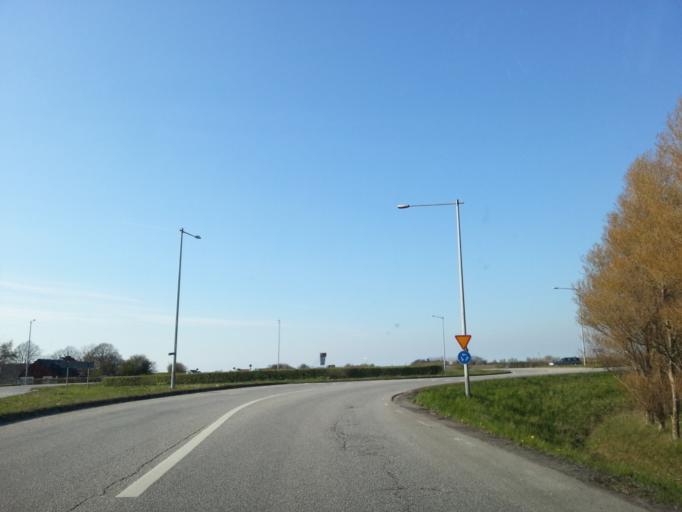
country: SE
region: Skane
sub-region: Vellinge Kommun
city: Hollviken
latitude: 55.4250
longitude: 12.9605
